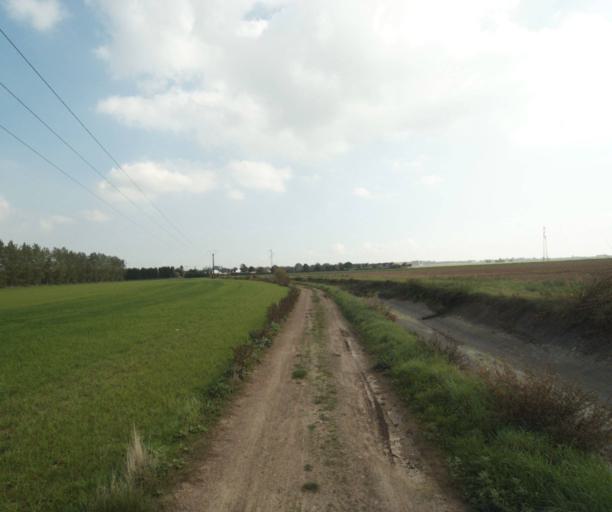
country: FR
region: Nord-Pas-de-Calais
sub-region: Departement du Nord
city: Houplin-Ancoisne
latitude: 50.5785
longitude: 3.0050
